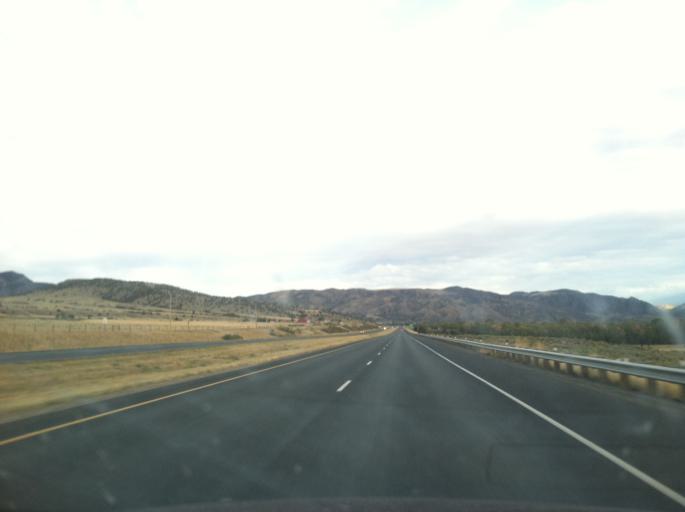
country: US
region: Montana
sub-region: Jefferson County
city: Whitehall
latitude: 45.8746
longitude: -111.9875
